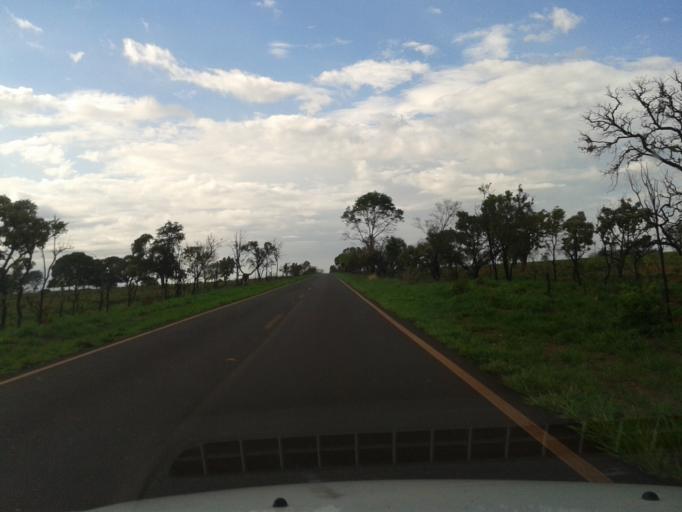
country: BR
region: Minas Gerais
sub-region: Ituiutaba
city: Ituiutaba
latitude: -19.0564
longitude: -49.7667
